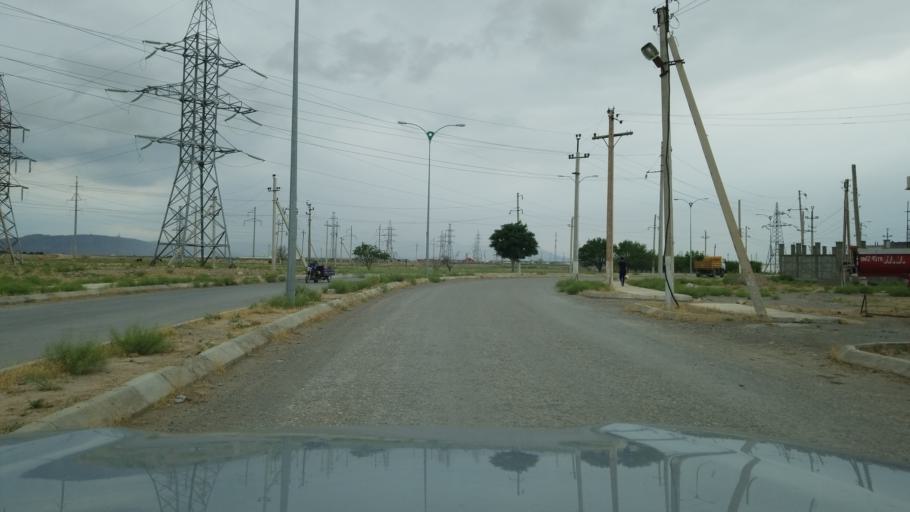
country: TM
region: Balkan
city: Serdar
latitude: 38.9715
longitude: 56.2554
